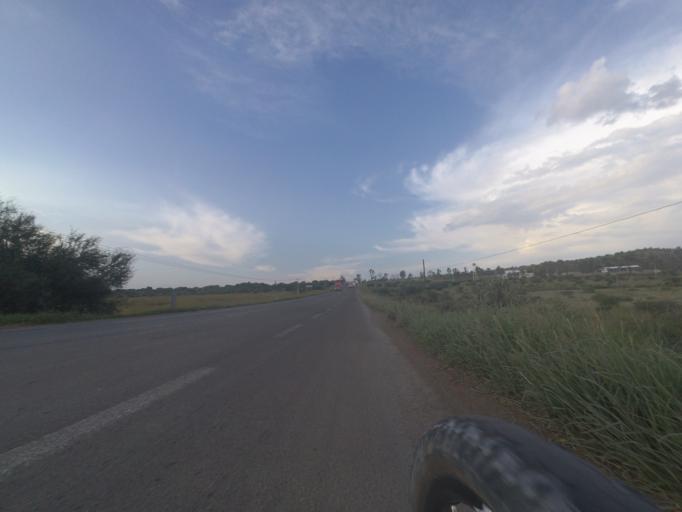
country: MX
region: Aguascalientes
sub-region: Aguascalientes
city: La Loma de los Negritos
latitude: 21.8351
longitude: -102.3764
